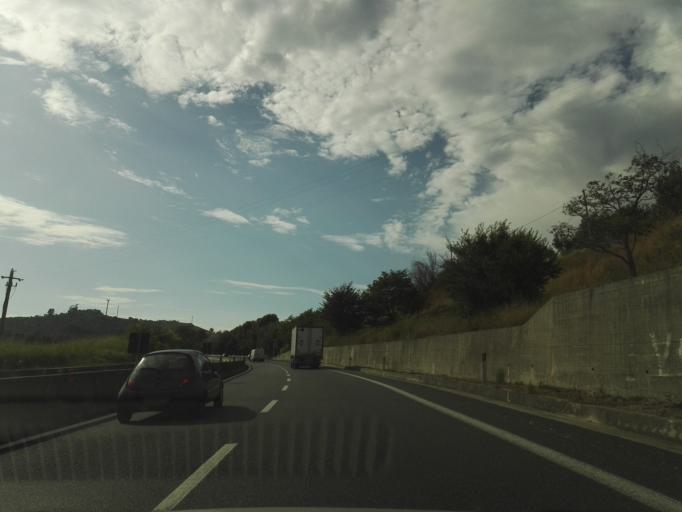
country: IT
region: Calabria
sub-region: Provincia di Catanzaro
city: Marcellinara
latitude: 38.9163
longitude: 16.4905
